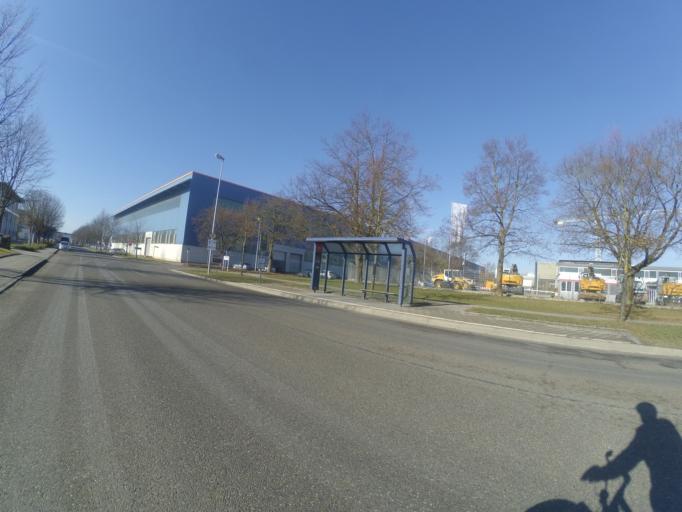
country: DE
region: Baden-Wuerttemberg
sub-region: Tuebingen Region
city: Ulm
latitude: 48.3613
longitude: 9.9465
